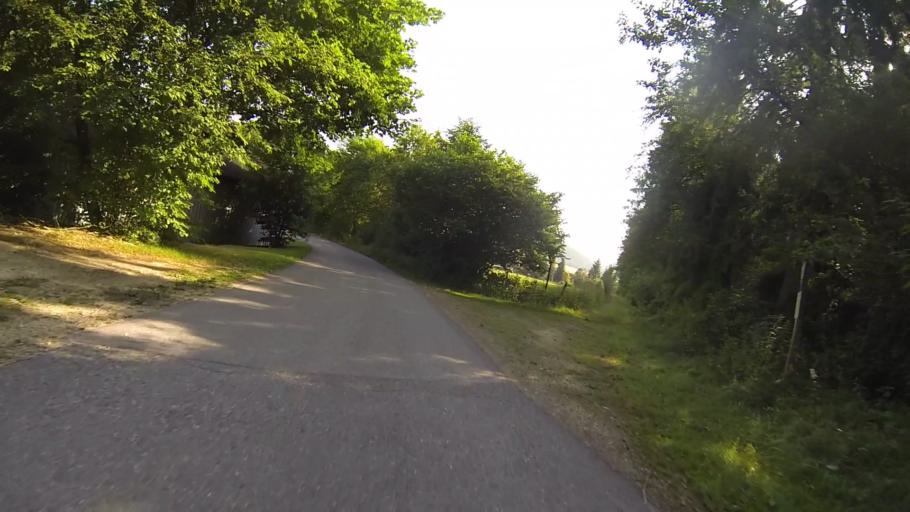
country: DE
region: Baden-Wuerttemberg
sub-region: Regierungsbezirk Stuttgart
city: Konigsbronn
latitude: 48.7270
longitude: 10.1339
